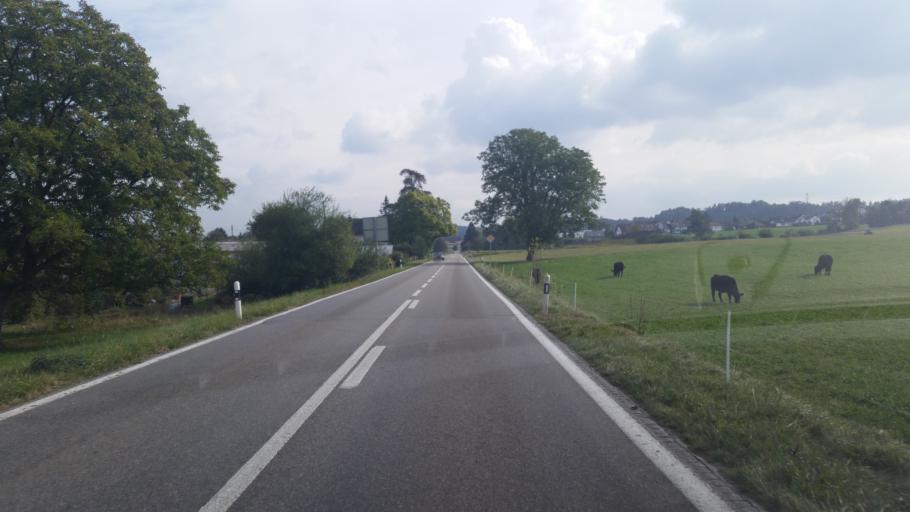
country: CH
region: Aargau
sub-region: Bezirk Baden
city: Kunten
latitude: 47.3832
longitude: 8.2986
